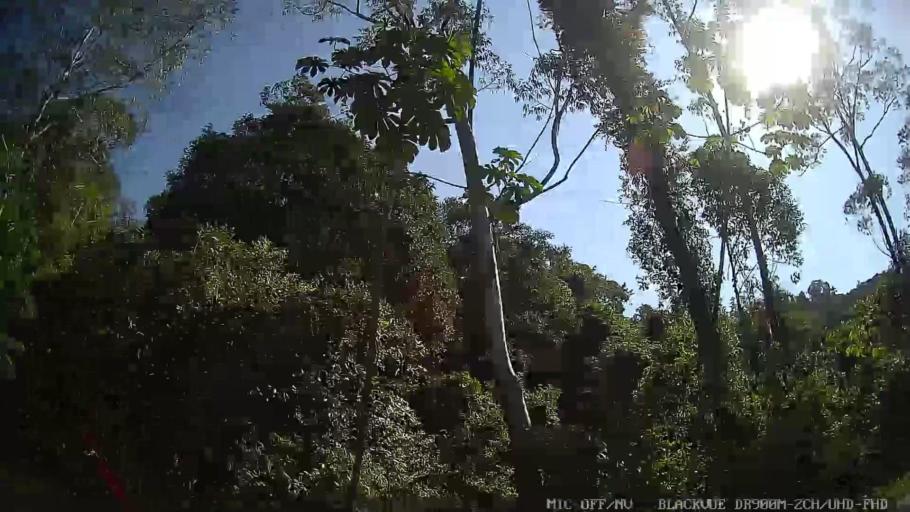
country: BR
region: Sao Paulo
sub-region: Bertioga
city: Bertioga
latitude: -23.8851
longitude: -46.2008
